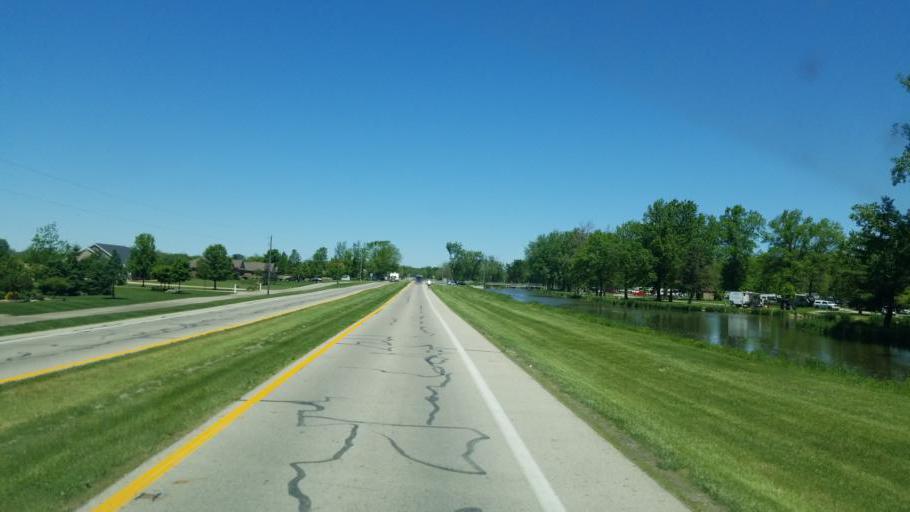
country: US
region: Ohio
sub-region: Shelby County
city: Fort Loramie
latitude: 40.3540
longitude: -84.3551
